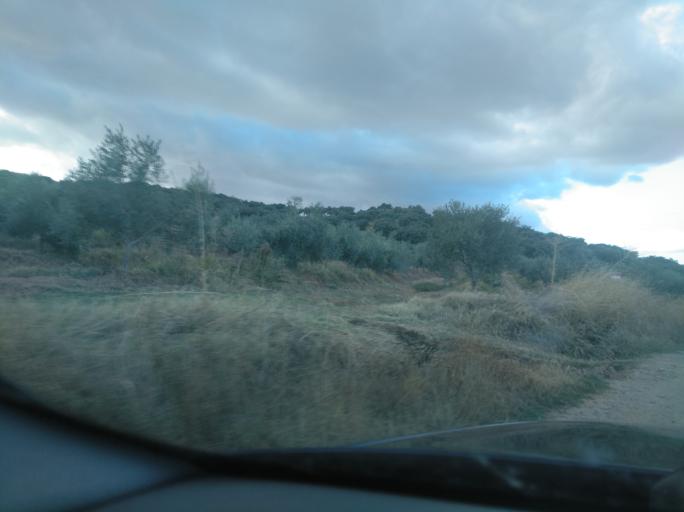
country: PT
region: Portalegre
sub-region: Campo Maior
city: Campo Maior
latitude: 39.0454
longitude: -6.9954
